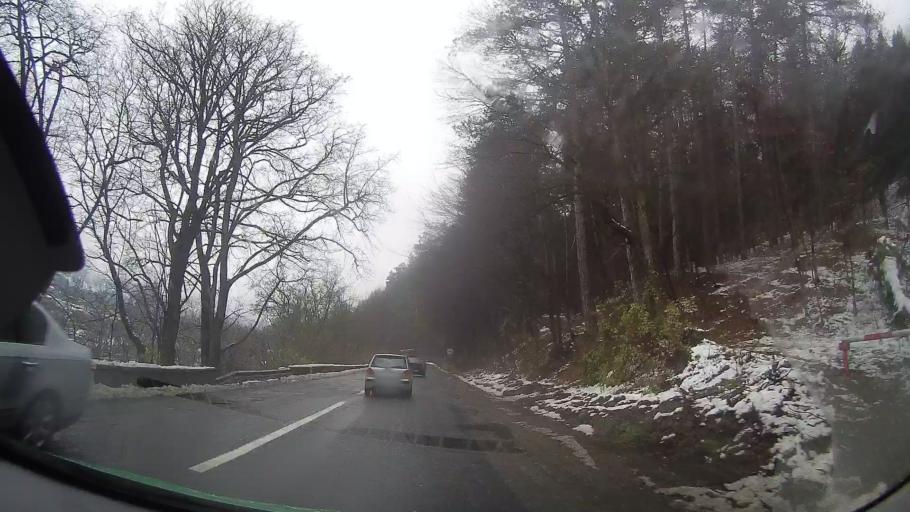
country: RO
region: Neamt
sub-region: Comuna Tarcau
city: Tarcau
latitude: 46.8966
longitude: 26.1222
